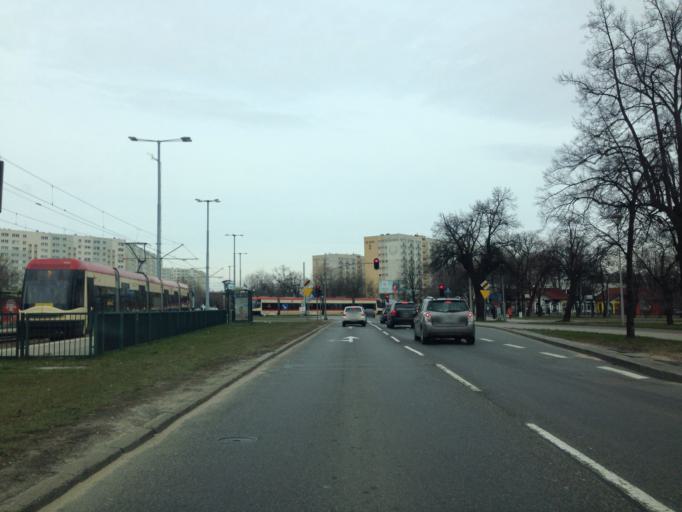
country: PL
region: Pomeranian Voivodeship
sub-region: Sopot
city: Sopot
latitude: 54.4192
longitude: 18.5848
